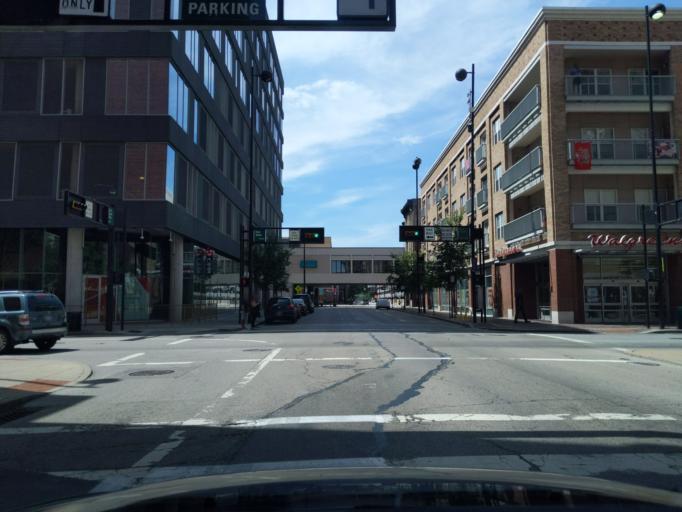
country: US
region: Kentucky
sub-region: Kenton County
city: Covington
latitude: 39.1023
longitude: -84.5144
